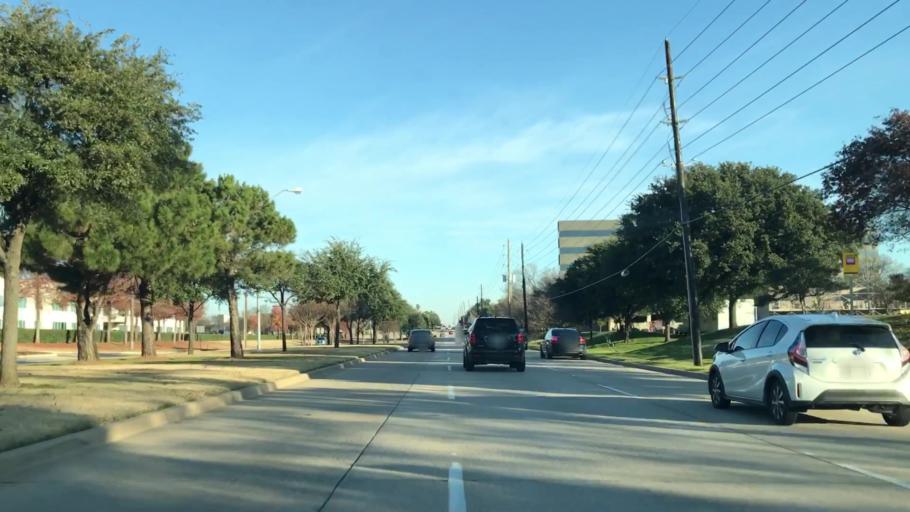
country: US
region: Texas
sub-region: Dallas County
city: Coppell
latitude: 32.9132
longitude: -96.9936
